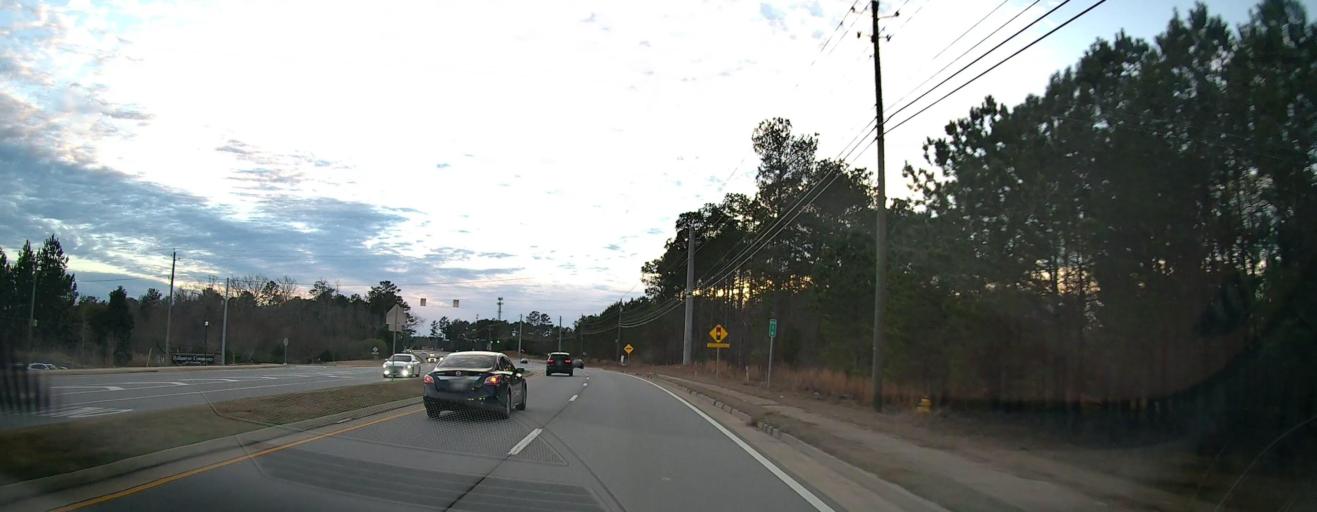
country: US
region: Alabama
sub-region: Russell County
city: Phenix City
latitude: 32.5694
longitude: -84.9308
